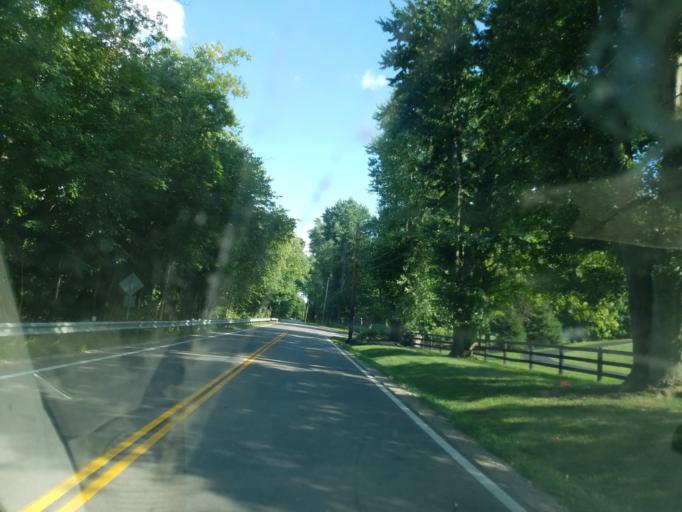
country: US
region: Ohio
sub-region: Delaware County
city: Powell
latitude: 40.1813
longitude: -83.0495
